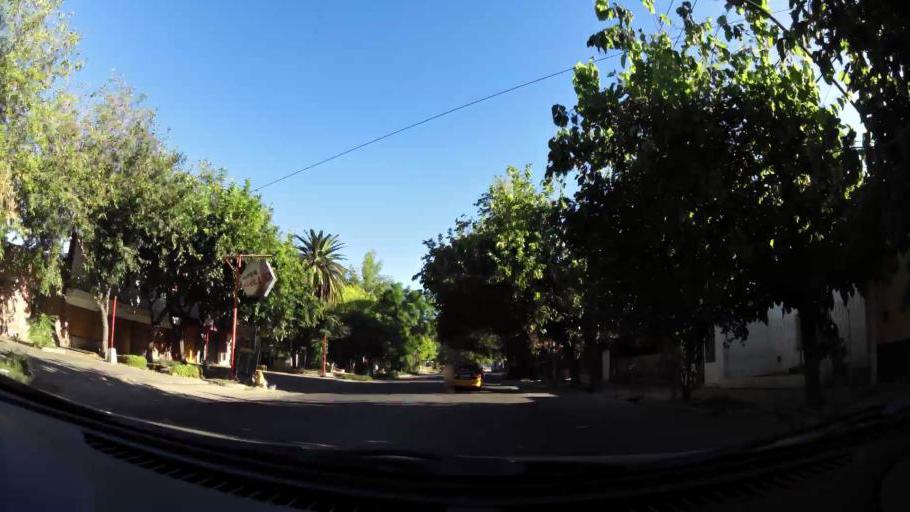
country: AR
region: Mendoza
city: Las Heras
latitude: -32.8654
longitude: -68.8288
